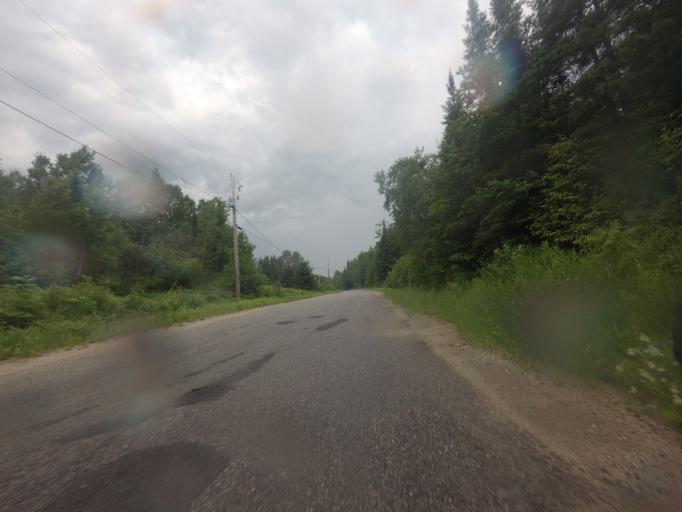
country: CA
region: Quebec
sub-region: Outaouais
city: Maniwaki
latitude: 46.4376
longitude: -75.9411
